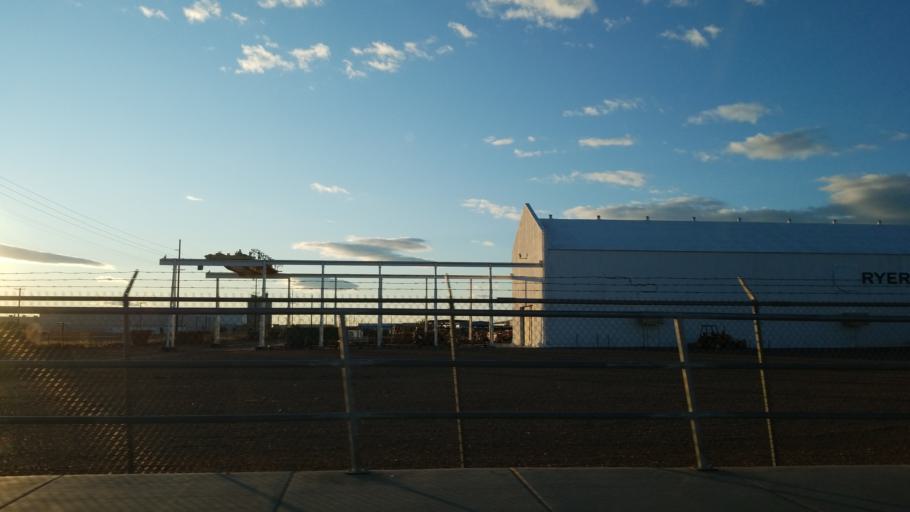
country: US
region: Arizona
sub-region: Maricopa County
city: Laveen
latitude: 33.4447
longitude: -112.1693
